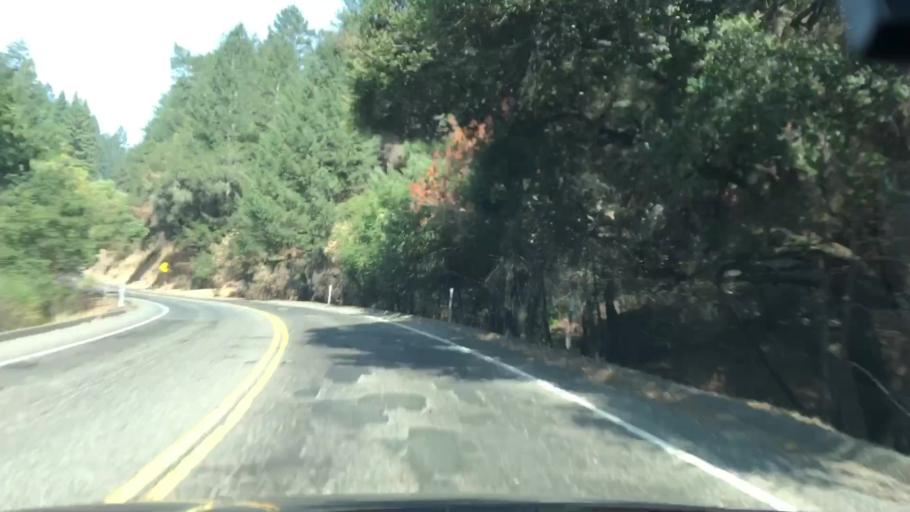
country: US
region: California
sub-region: Napa County
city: Calistoga
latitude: 38.5522
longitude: -122.6511
